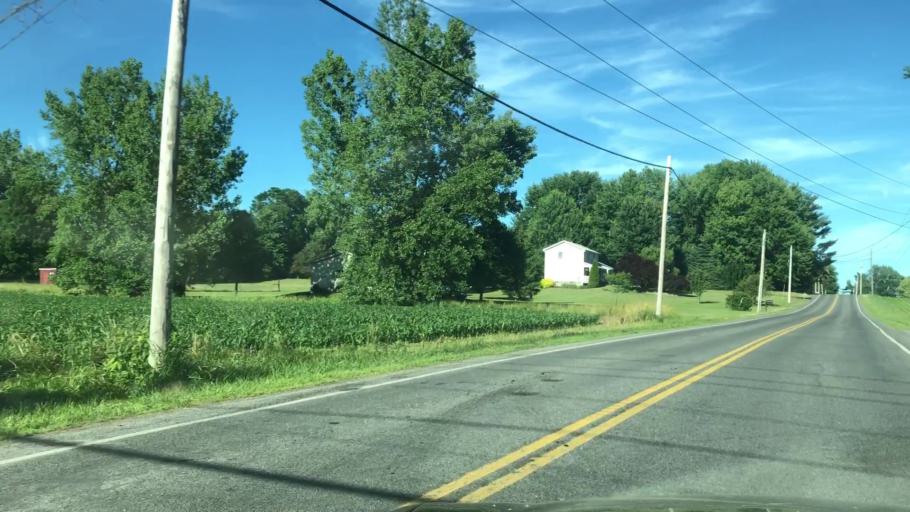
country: US
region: New York
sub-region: Wayne County
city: Macedon
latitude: 43.1164
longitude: -77.3207
